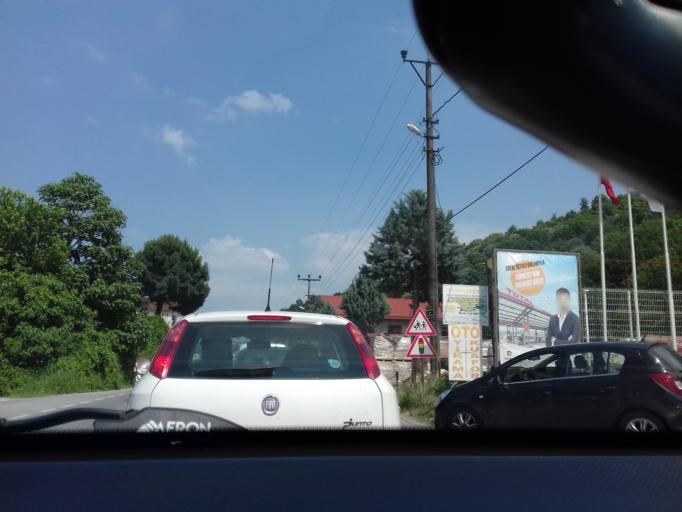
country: TR
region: Sakarya
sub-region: Merkez
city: Sapanca
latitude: 40.6908
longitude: 30.2219
